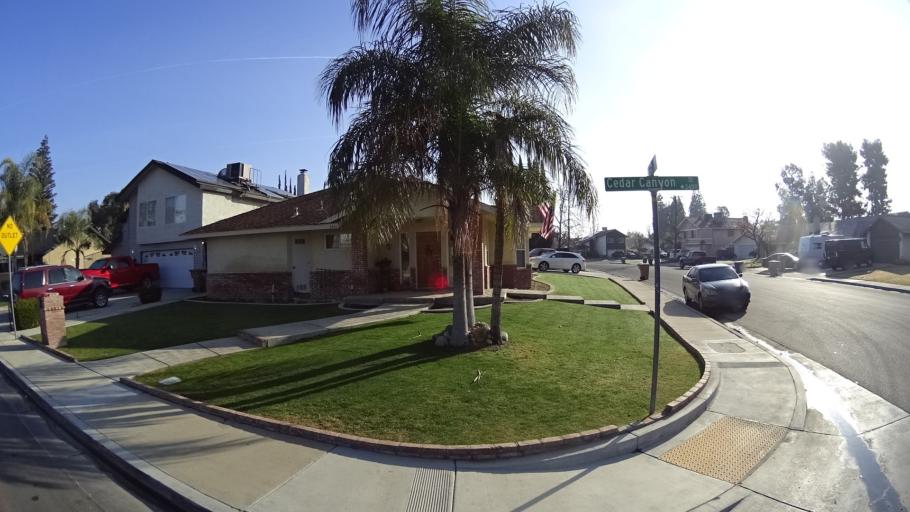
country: US
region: California
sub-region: Kern County
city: Oildale
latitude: 35.4039
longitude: -118.9335
